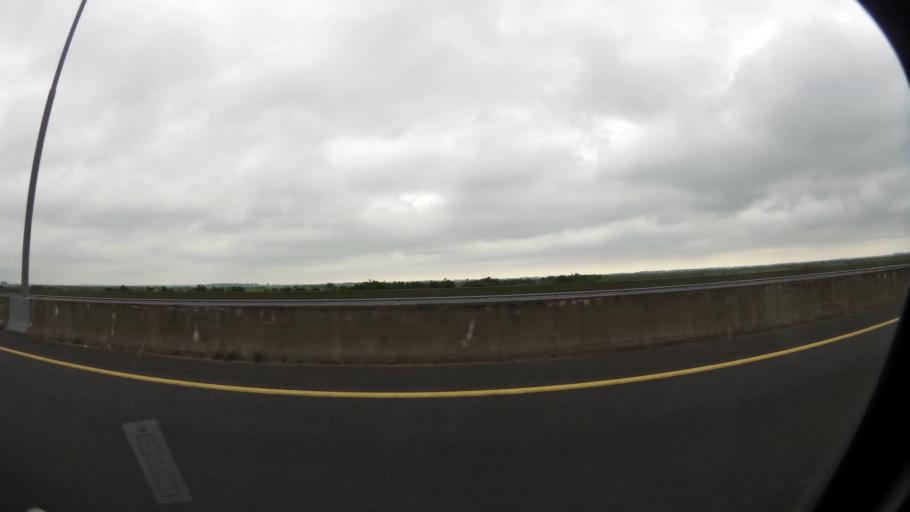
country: AR
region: Buenos Aires
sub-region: Partido de La Plata
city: La Plata
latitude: -34.8608
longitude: -58.0208
